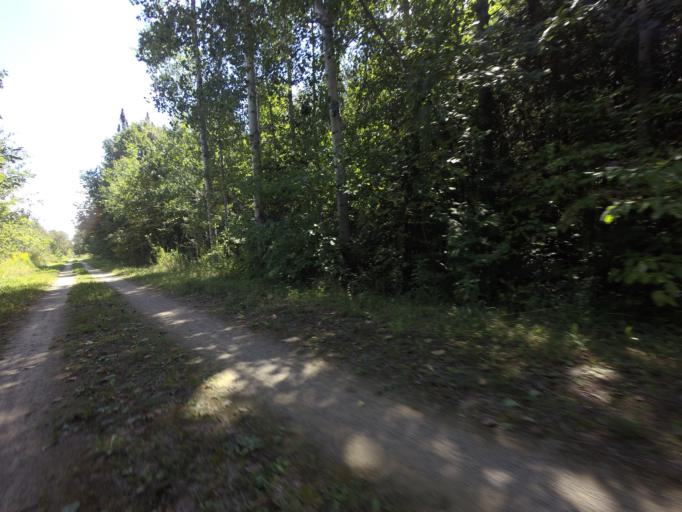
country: CA
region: Ontario
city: Orangeville
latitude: 43.7775
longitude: -80.2061
